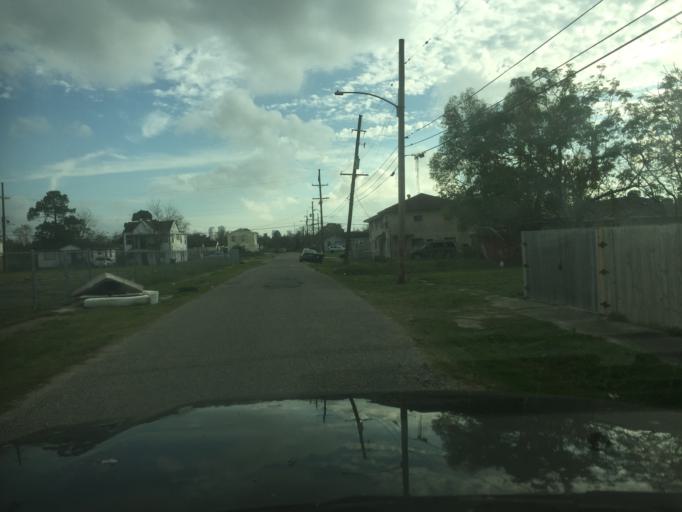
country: US
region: Louisiana
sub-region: Orleans Parish
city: New Orleans
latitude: 29.9954
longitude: -90.0806
